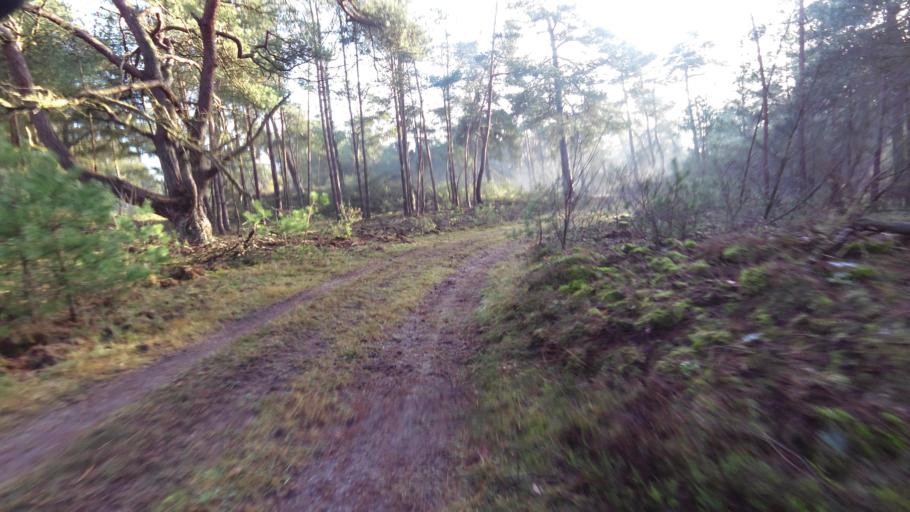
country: NL
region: Gelderland
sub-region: Gemeente Barneveld
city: Garderen
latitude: 52.1996
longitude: 5.7414
